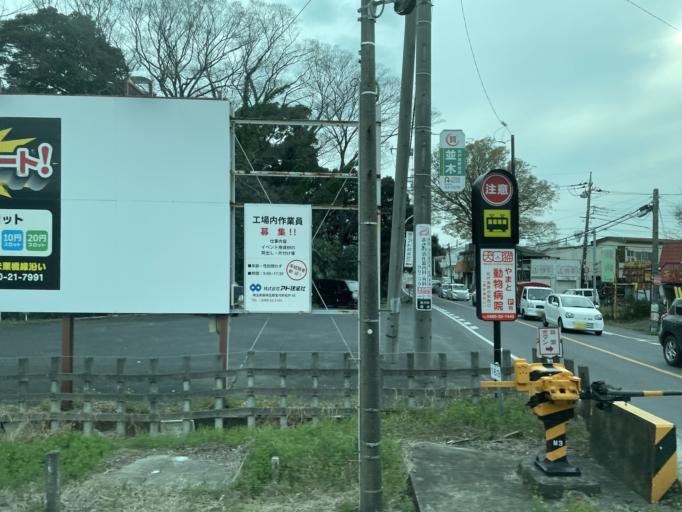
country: JP
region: Saitama
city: Sugito
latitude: 36.0420
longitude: 139.6980
